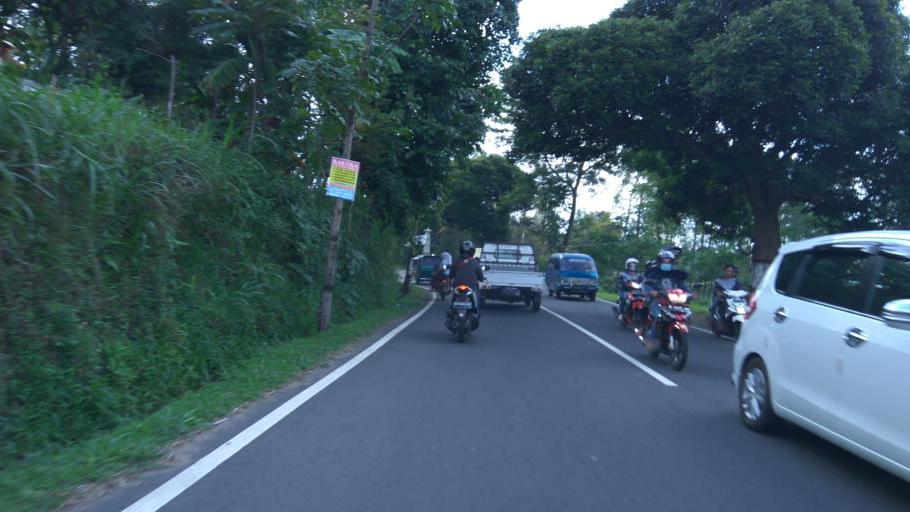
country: ID
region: Central Java
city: Salatiga
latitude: -7.3692
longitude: 110.4535
